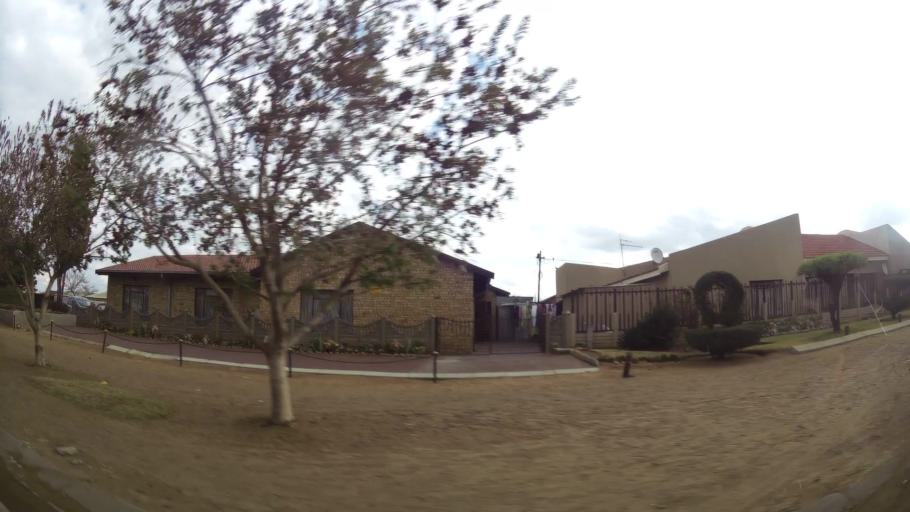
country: ZA
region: Orange Free State
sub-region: Fezile Dabi District Municipality
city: Sasolburg
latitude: -26.8454
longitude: 27.8468
